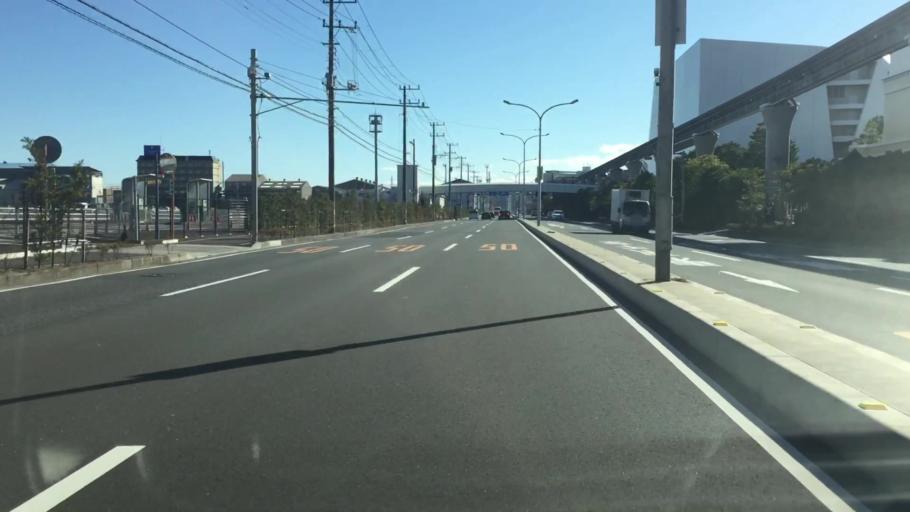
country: JP
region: Tokyo
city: Urayasu
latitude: 35.6344
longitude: 139.8881
